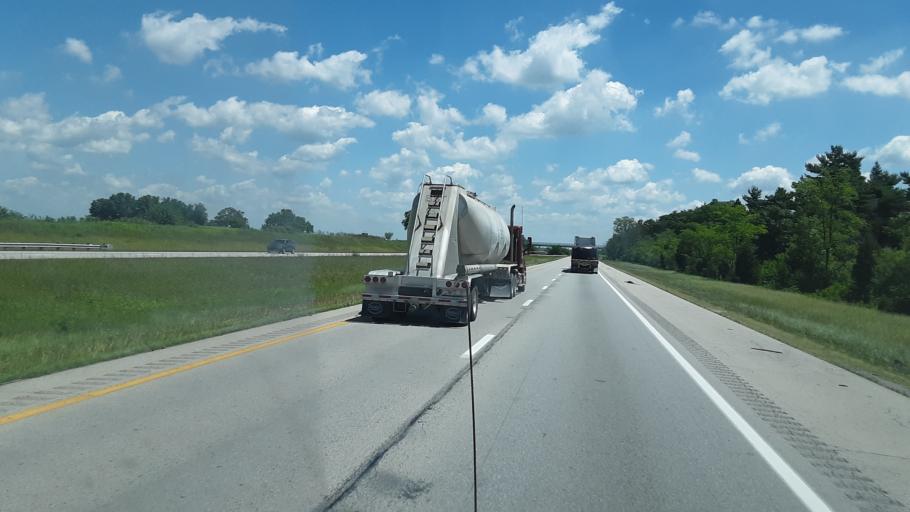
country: US
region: Ohio
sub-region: Clinton County
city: Wilmington
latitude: 39.5348
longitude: -83.7869
